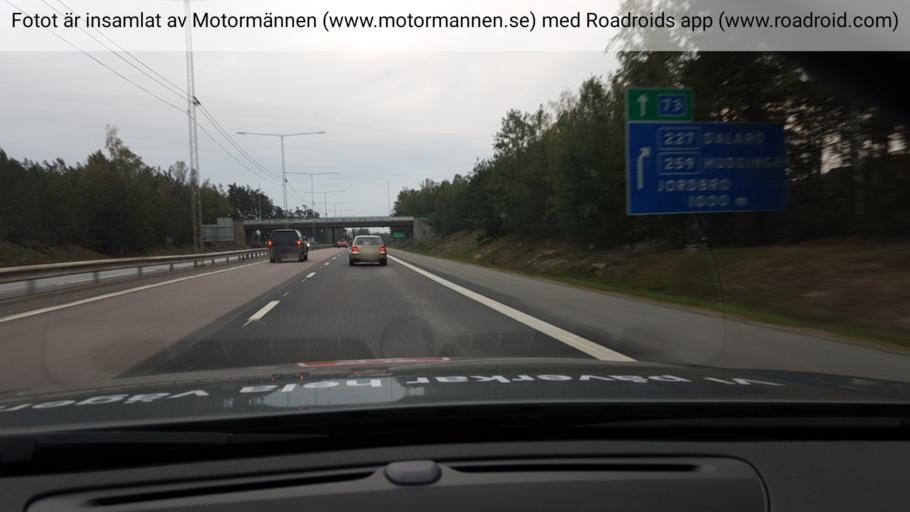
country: SE
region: Stockholm
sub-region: Haninge Kommun
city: Haninge
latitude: 59.1696
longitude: 18.1590
